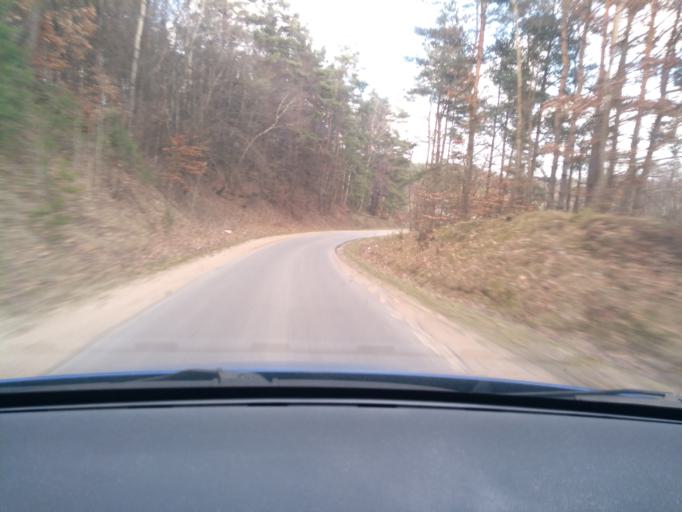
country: PL
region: Pomeranian Voivodeship
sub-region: Powiat kartuski
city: Przodkowo
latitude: 54.4143
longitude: 18.2394
